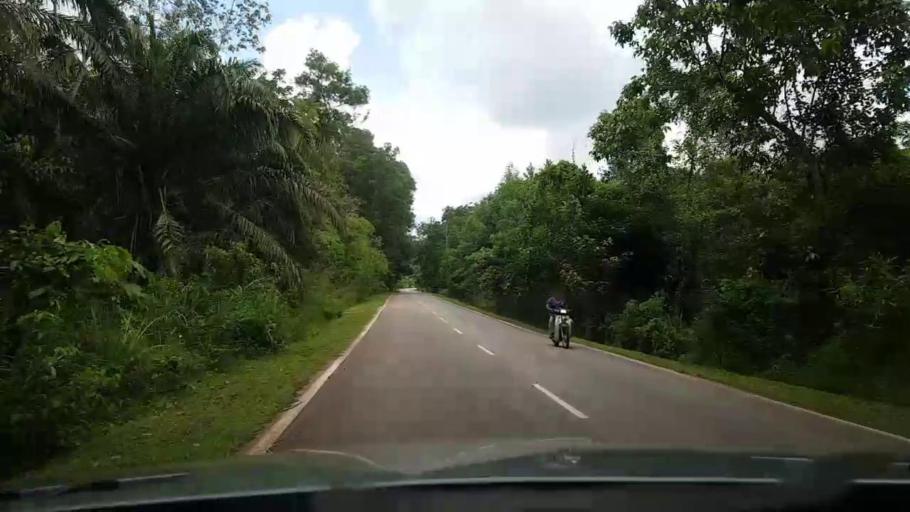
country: MY
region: Pahang
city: Pekan
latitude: 3.1490
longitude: 102.9705
